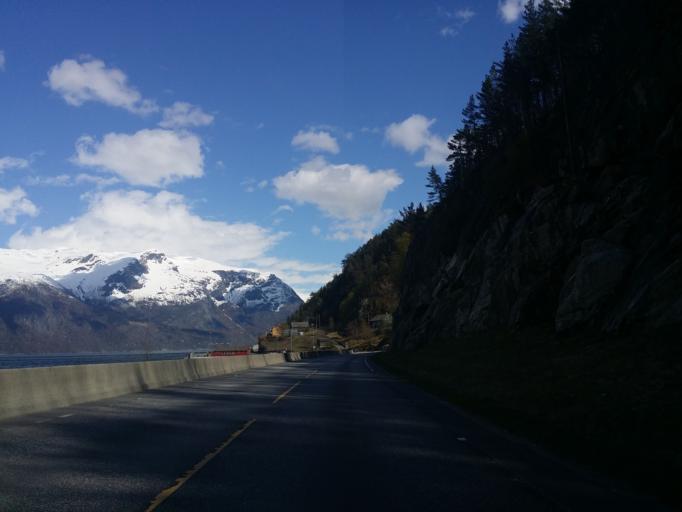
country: NO
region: Hordaland
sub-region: Ulvik
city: Ulvik
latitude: 60.4700
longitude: 6.9025
